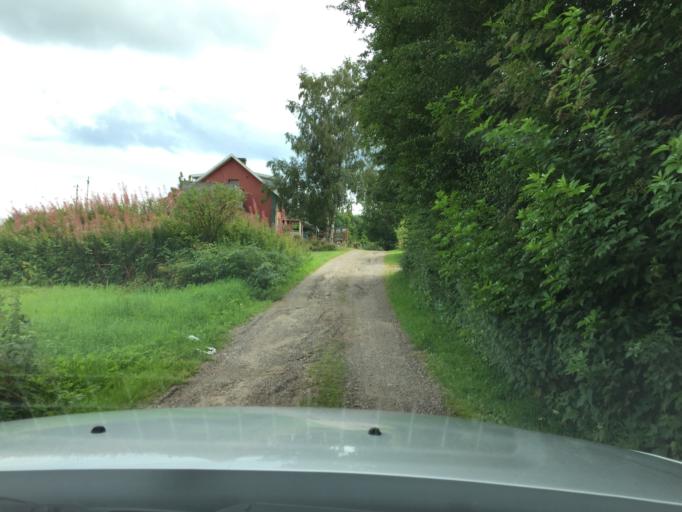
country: SE
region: Skane
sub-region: Hassleholms Kommun
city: Sosdala
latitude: 56.0098
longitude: 13.6405
